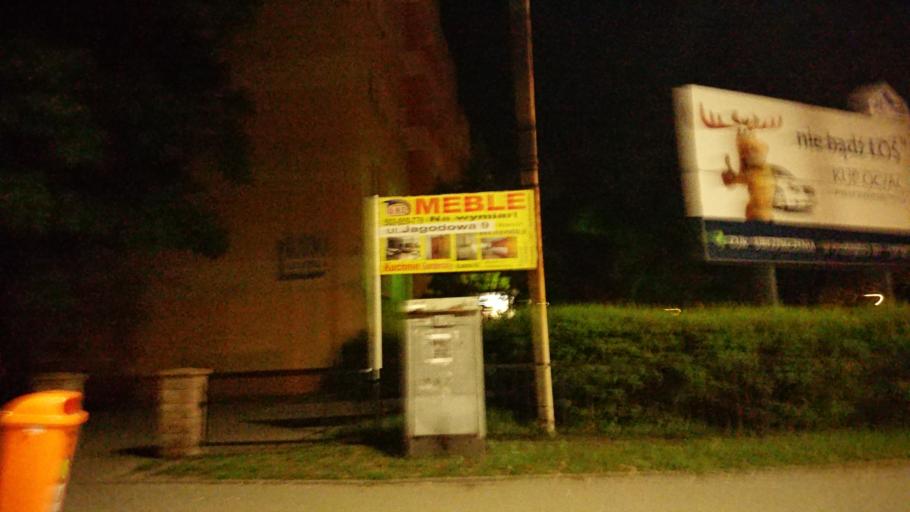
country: PL
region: Kujawsko-Pomorskie
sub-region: Torun
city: Torun
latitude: 53.0245
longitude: 18.6016
